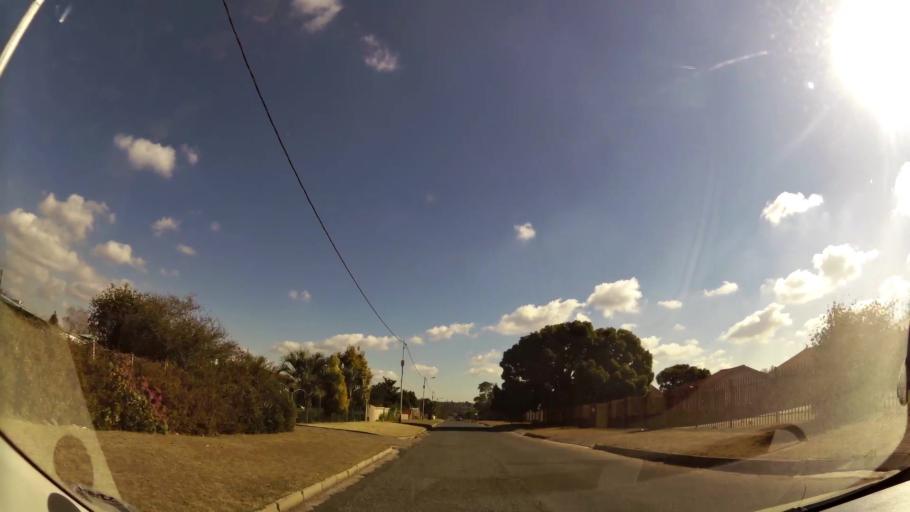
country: ZA
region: Gauteng
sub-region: City of Johannesburg Metropolitan Municipality
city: Roodepoort
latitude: -26.1450
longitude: 27.8281
